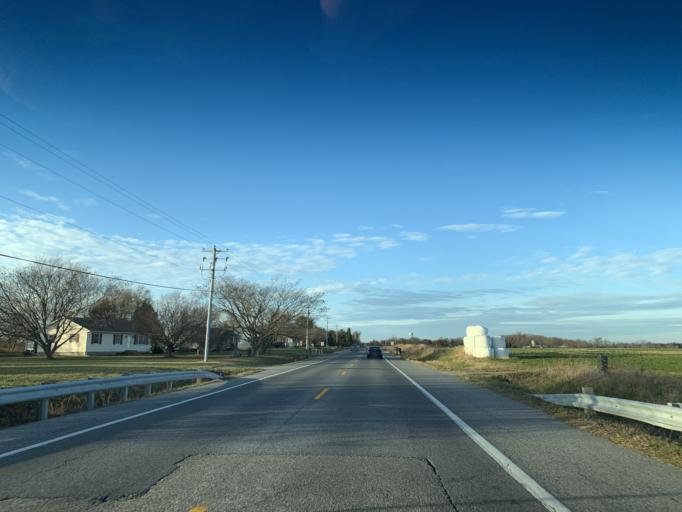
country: US
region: Maryland
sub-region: Kent County
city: Chestertown
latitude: 39.2639
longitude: -76.0870
